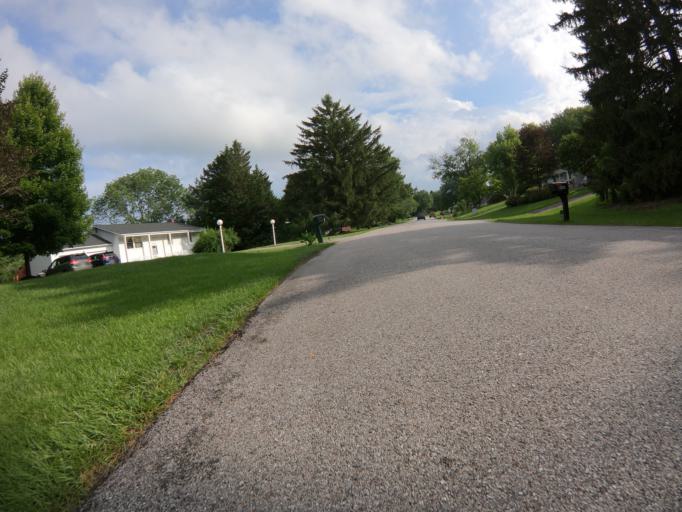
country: US
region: Maryland
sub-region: Howard County
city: Ellicott City
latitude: 39.2554
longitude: -76.8072
